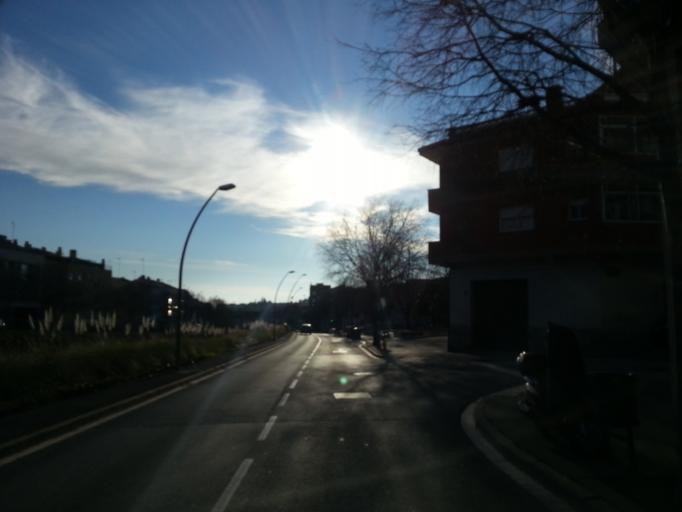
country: ES
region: Catalonia
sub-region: Provincia de Barcelona
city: Terrassa
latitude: 41.5793
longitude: 2.0058
